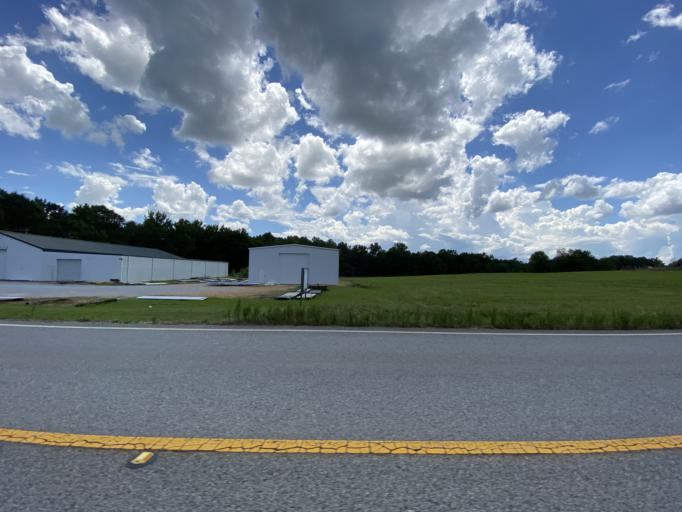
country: US
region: Alabama
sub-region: Lauderdale County
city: Underwood-Petersville
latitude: 34.9392
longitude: -87.8554
